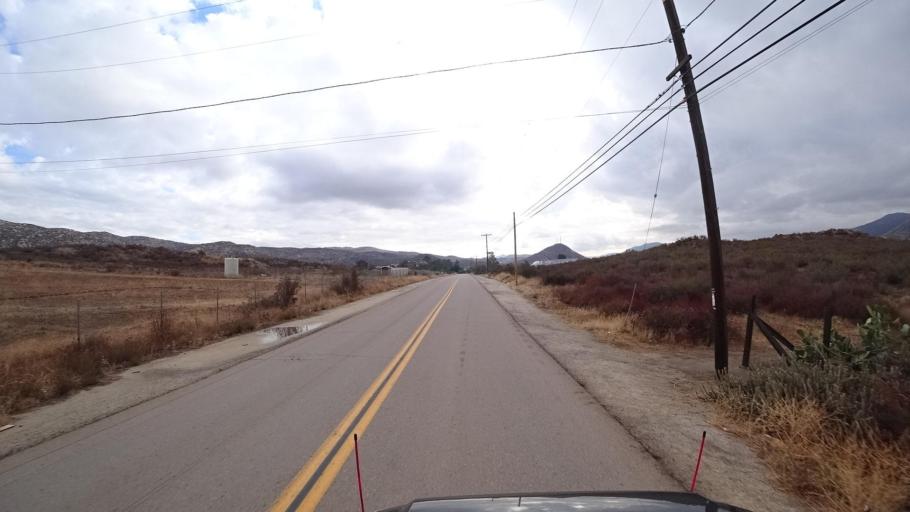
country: MX
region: Baja California
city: Tecate
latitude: 32.5827
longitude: -116.6263
